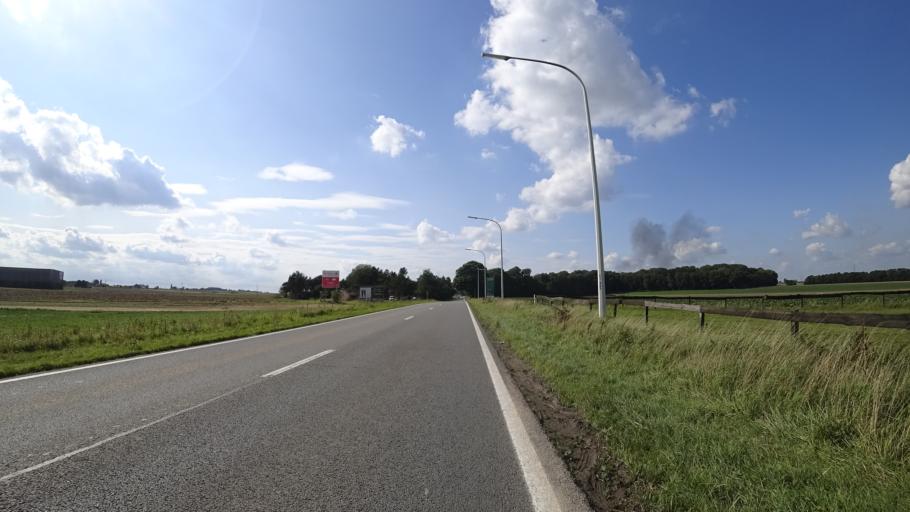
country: BE
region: Wallonia
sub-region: Province de Namur
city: Floreffe
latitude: 50.4885
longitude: 4.7504
